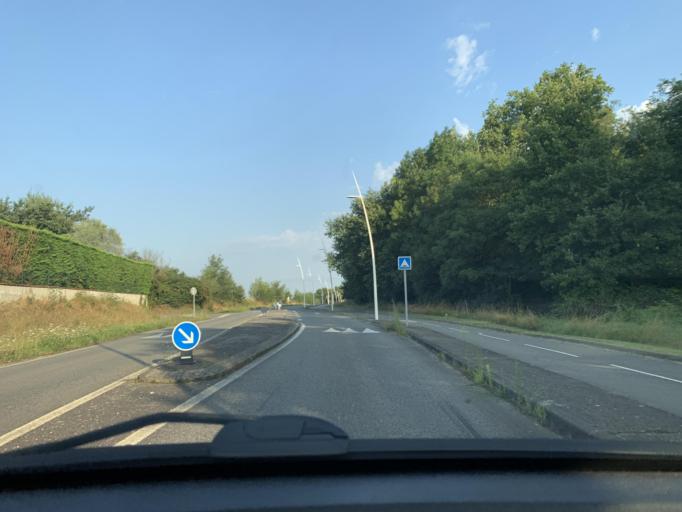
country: FR
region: Midi-Pyrenees
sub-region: Departement de la Haute-Garonne
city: Labege
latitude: 43.5344
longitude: 1.5431
